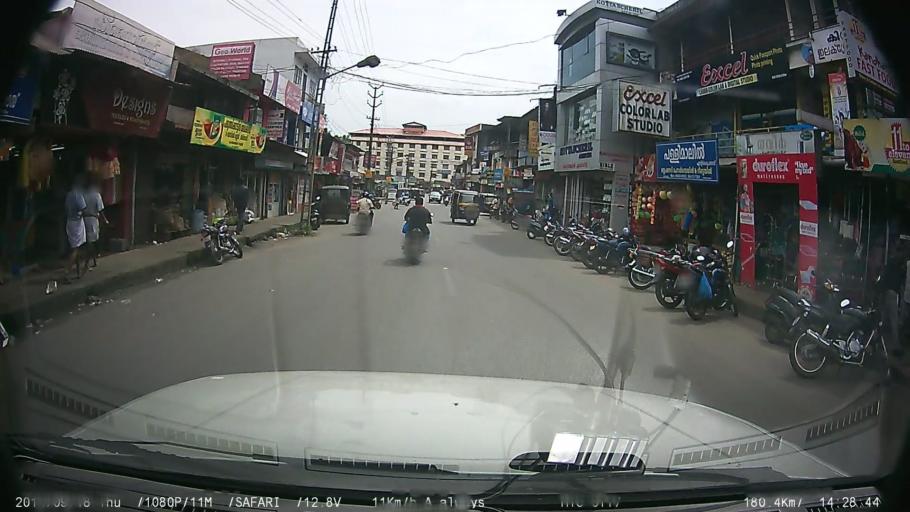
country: IN
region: Kerala
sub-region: Ernakulam
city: Kotamangalam
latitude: 10.0636
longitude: 76.6217
